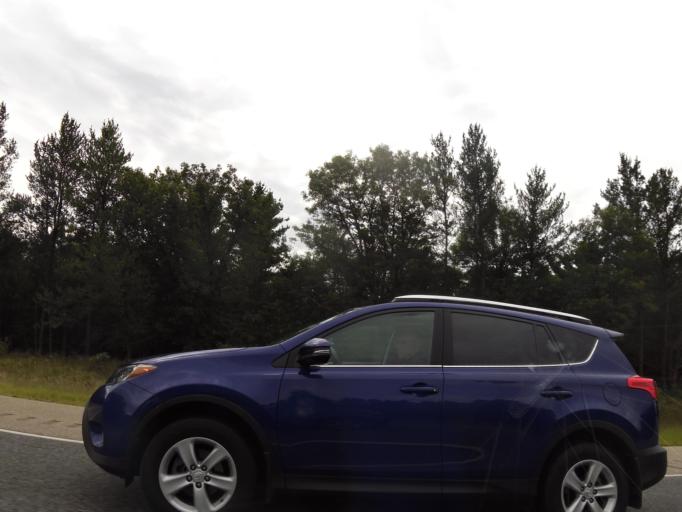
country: US
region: Wisconsin
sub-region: Monroe County
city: Sparta
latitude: 43.9407
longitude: -90.6636
